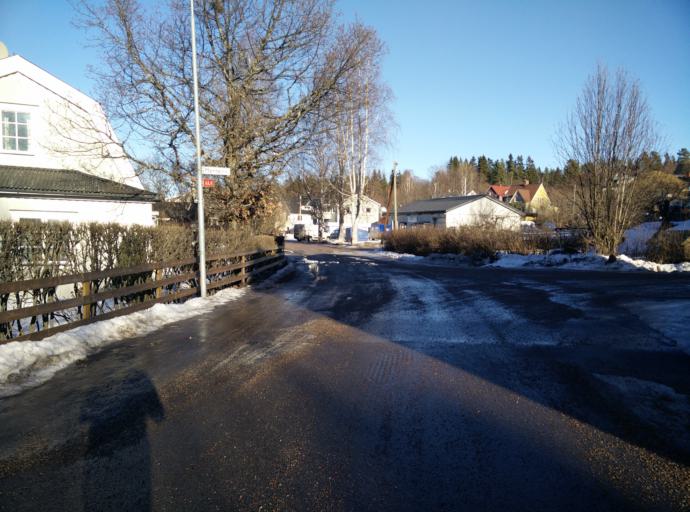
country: SE
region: Vaesternorrland
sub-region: Sundsvalls Kommun
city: Skottsund
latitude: 62.3060
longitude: 17.3862
